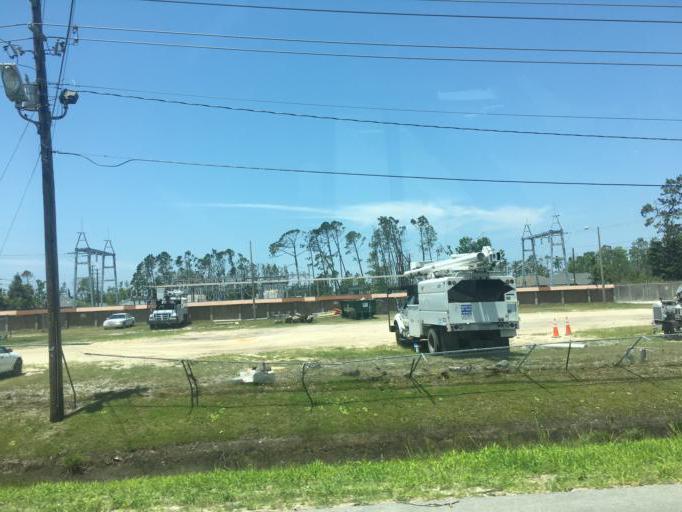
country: US
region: Florida
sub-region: Bay County
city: Pretty Bayou
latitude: 30.2127
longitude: -85.6664
